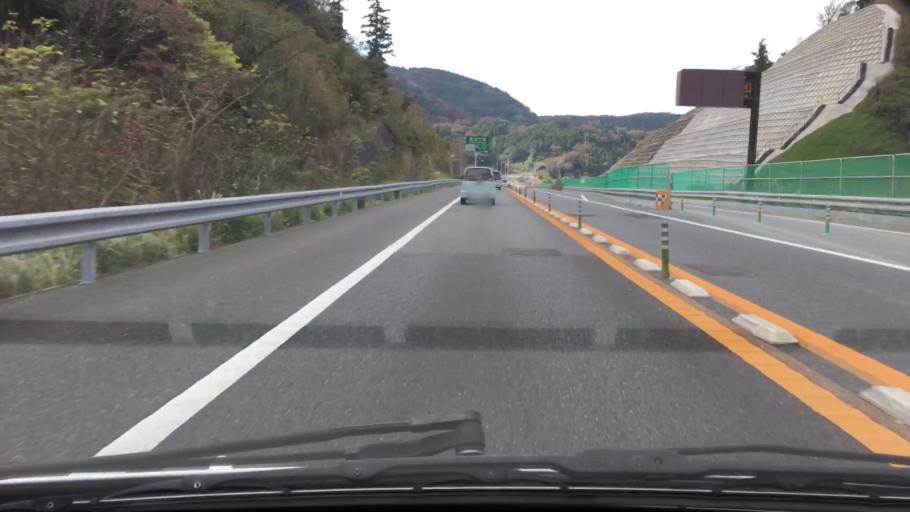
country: JP
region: Chiba
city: Futtsu
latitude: 35.1983
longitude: 139.8640
